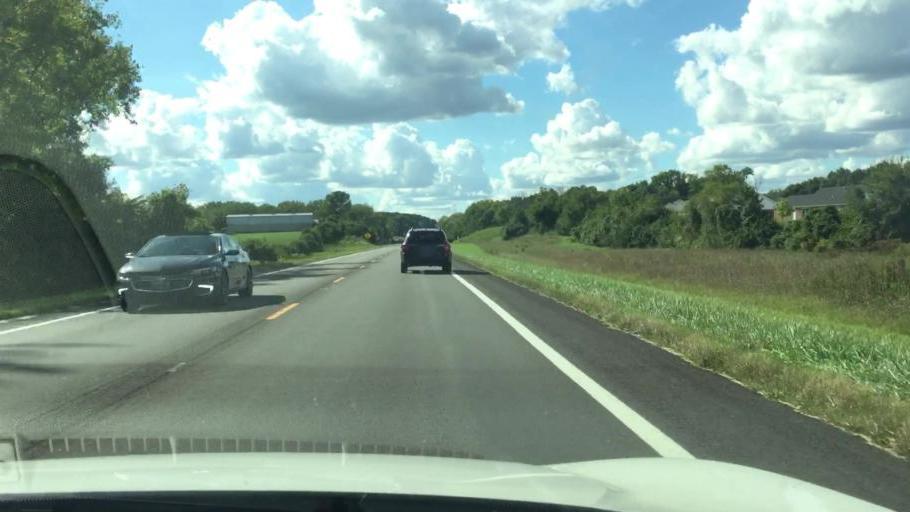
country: US
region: Ohio
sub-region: Clark County
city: Northridge
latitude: 39.9787
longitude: -83.7784
